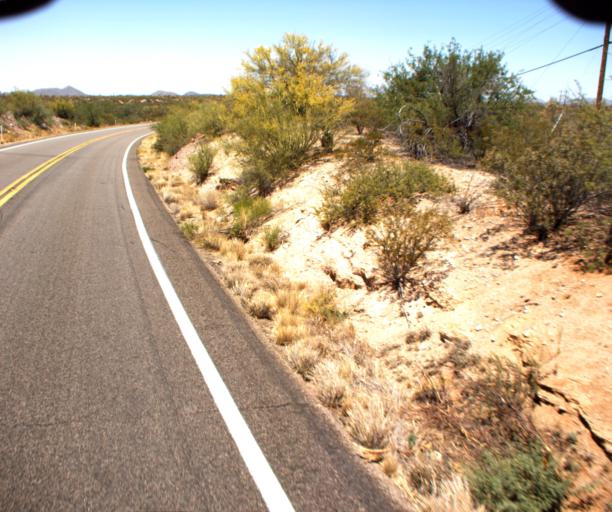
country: US
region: Arizona
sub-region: Pima County
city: Catalina
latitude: 32.6745
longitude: -111.0671
